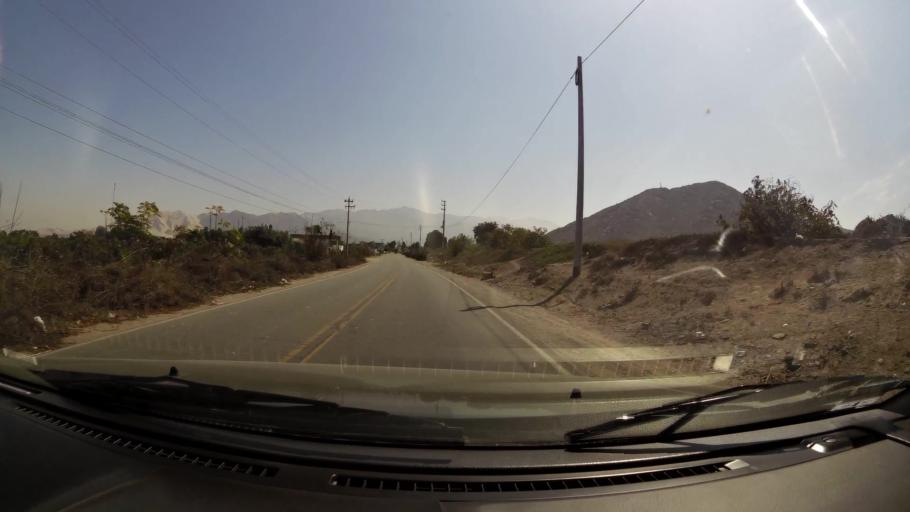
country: PE
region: Ica
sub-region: Provincia de Ica
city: San Juan Bautista
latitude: -13.9654
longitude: -75.6948
